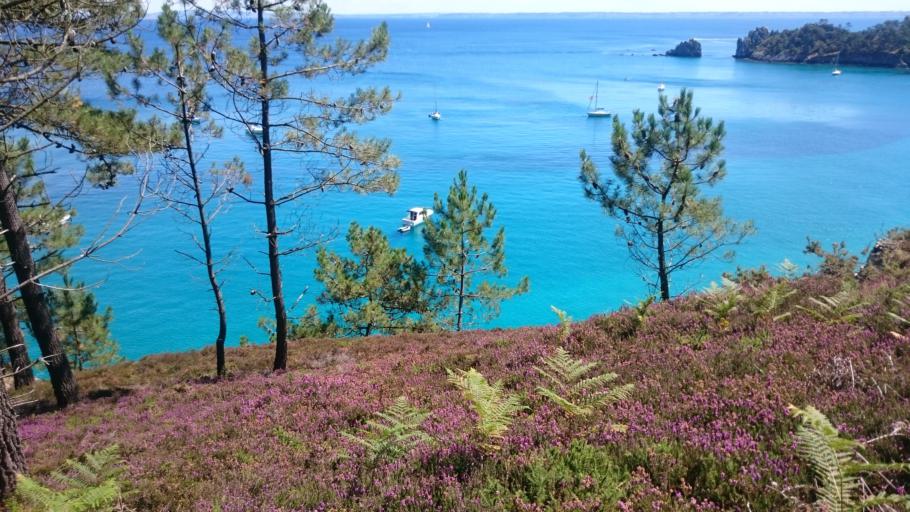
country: FR
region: Brittany
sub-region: Departement du Finistere
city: Crozon
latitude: 48.2067
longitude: -4.5145
